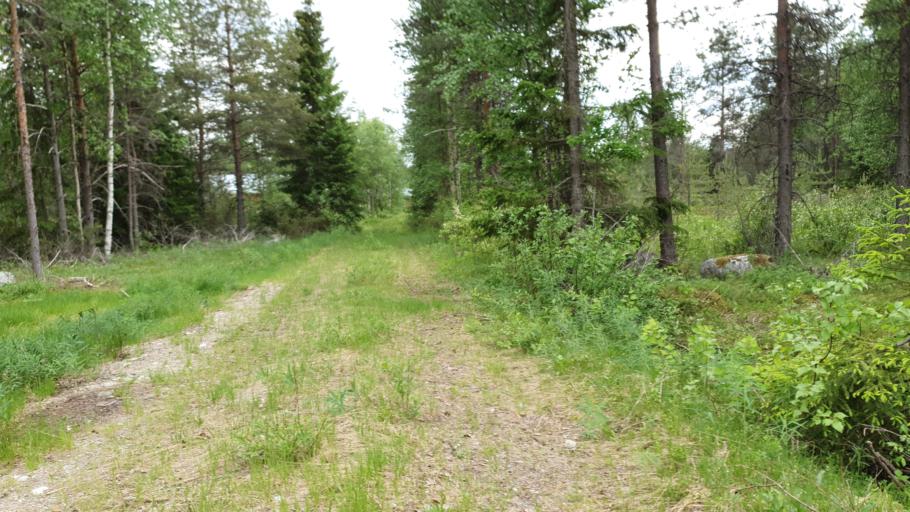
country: FI
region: Kainuu
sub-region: Kehys-Kainuu
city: Kuhmo
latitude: 64.4497
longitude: 29.6663
